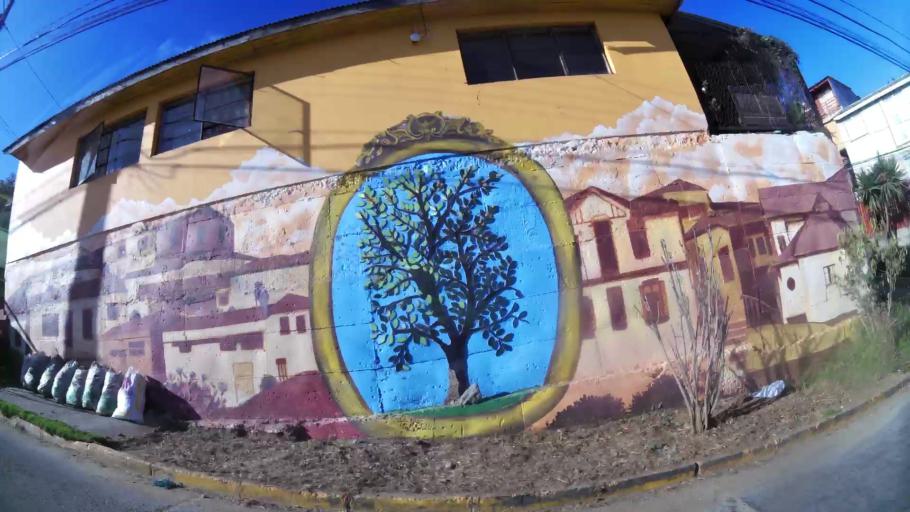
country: CL
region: Valparaiso
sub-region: Provincia de Valparaiso
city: Valparaiso
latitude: -33.0567
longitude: -71.6106
